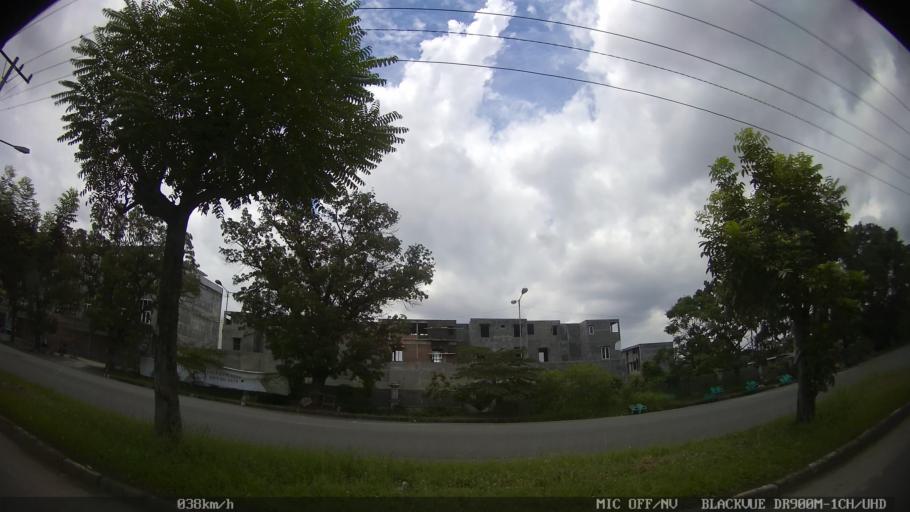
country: ID
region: North Sumatra
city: Medan
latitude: 3.6124
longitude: 98.7123
